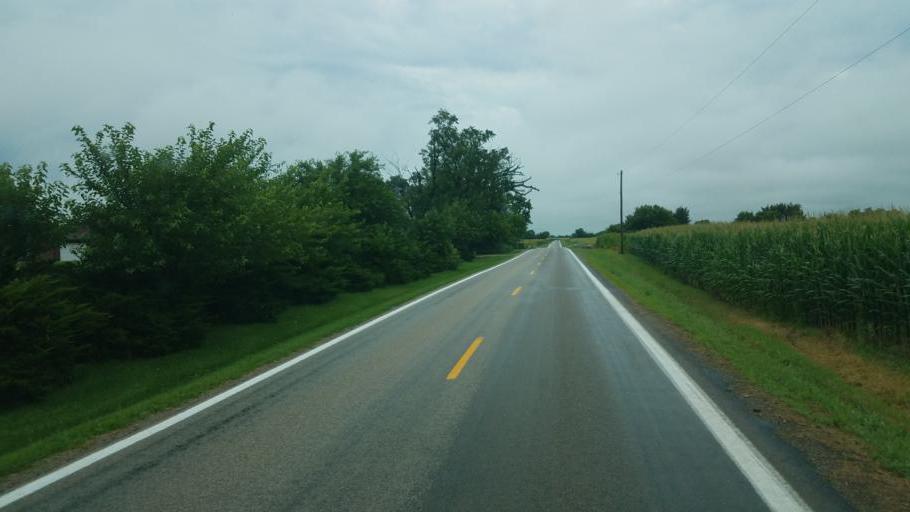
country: US
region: Ohio
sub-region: Union County
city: Richwood
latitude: 40.5298
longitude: -83.3519
